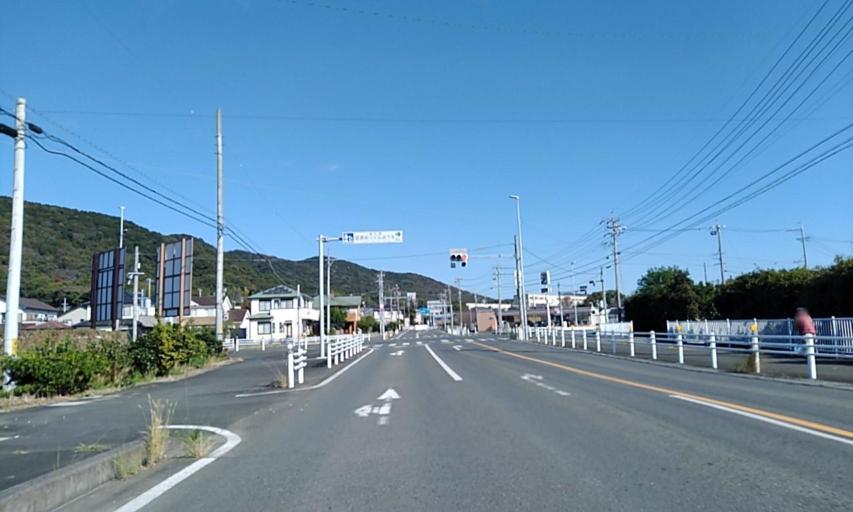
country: JP
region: Aichi
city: Tahara
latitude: 34.6529
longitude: 137.2431
